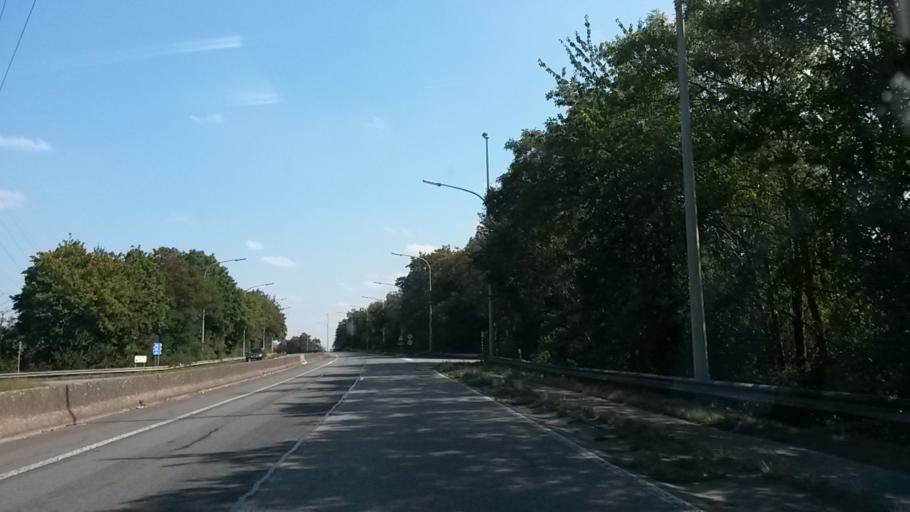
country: BE
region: Wallonia
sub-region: Province du Hainaut
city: Aiseau
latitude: 50.4467
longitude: 4.5934
